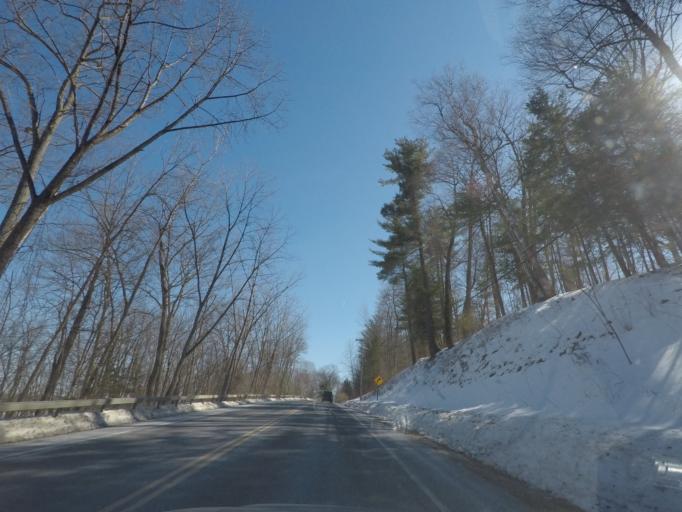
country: US
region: New York
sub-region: Saratoga County
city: Saratoga Springs
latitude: 43.0526
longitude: -73.7510
